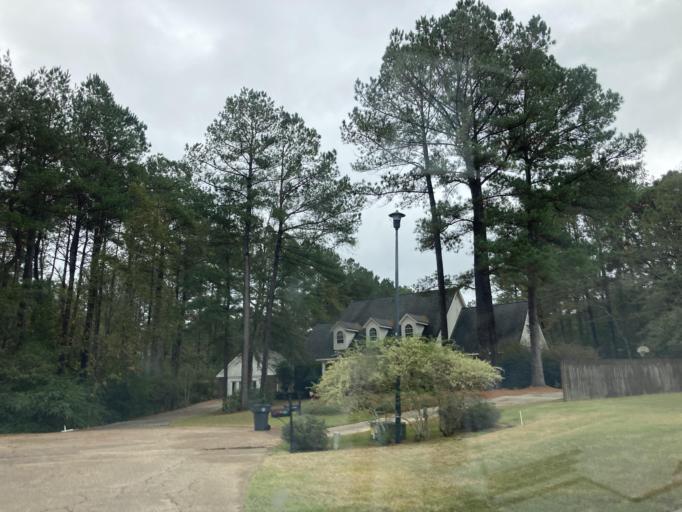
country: US
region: Mississippi
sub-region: Lamar County
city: West Hattiesburg
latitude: 31.2901
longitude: -89.4624
